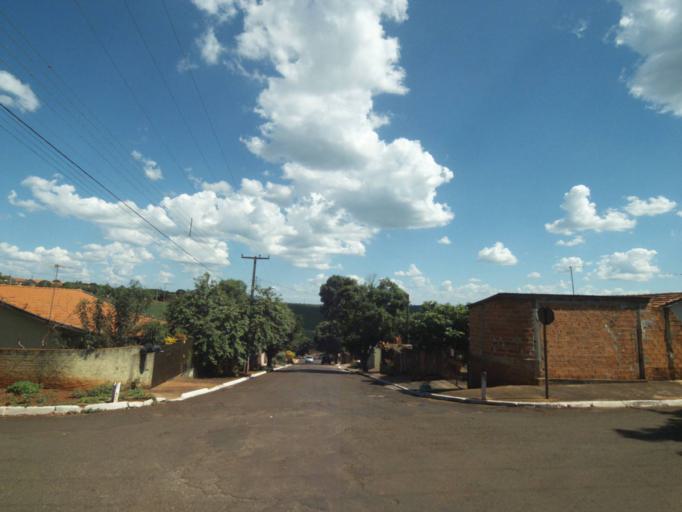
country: BR
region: Parana
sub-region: Sertanopolis
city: Sertanopolis
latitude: -23.0451
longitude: -50.8216
